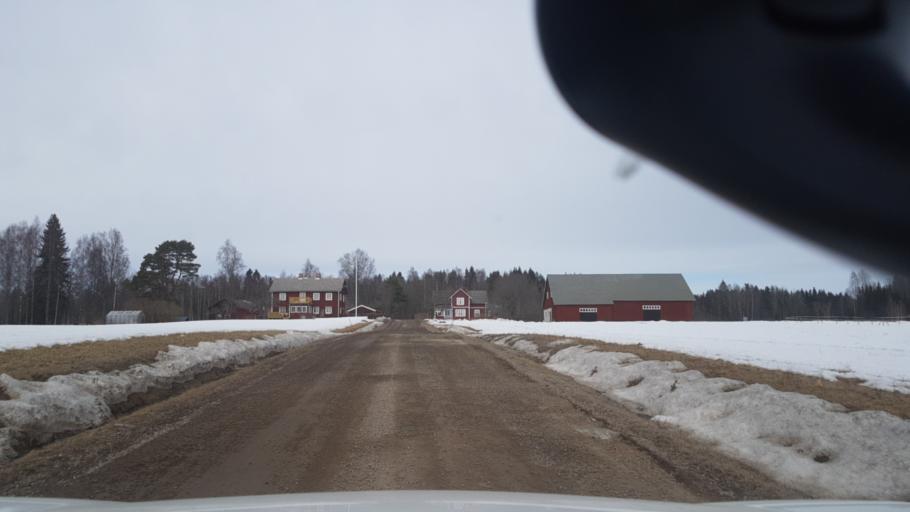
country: SE
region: Vaermland
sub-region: Eda Kommun
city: Amotfors
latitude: 59.7910
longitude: 12.4432
